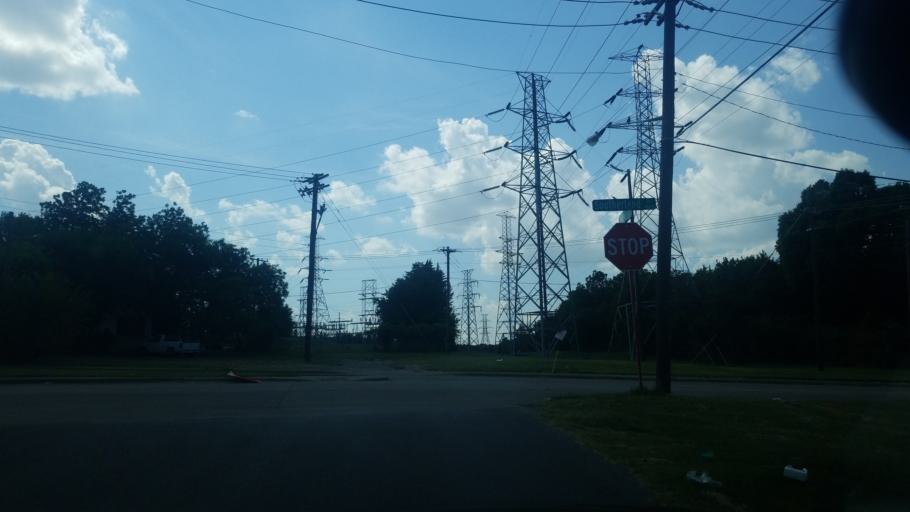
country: US
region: Texas
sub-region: Dallas County
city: Dallas
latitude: 32.7215
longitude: -96.8004
